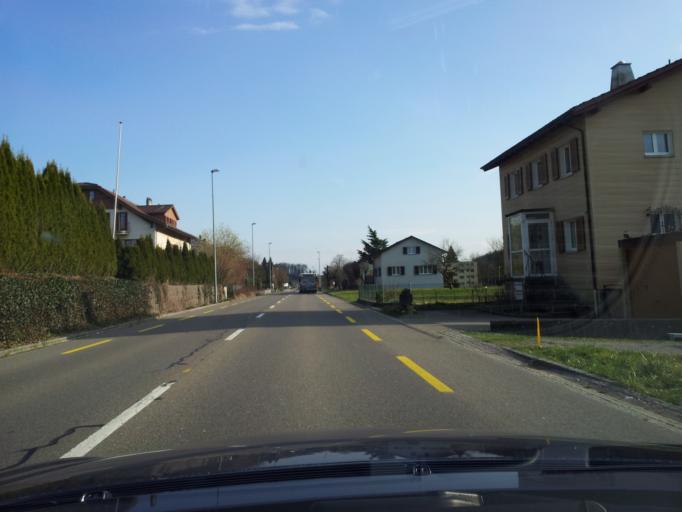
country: CH
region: Aargau
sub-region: Bezirk Baden
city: Niederrohrdorf
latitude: 47.4402
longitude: 8.2968
